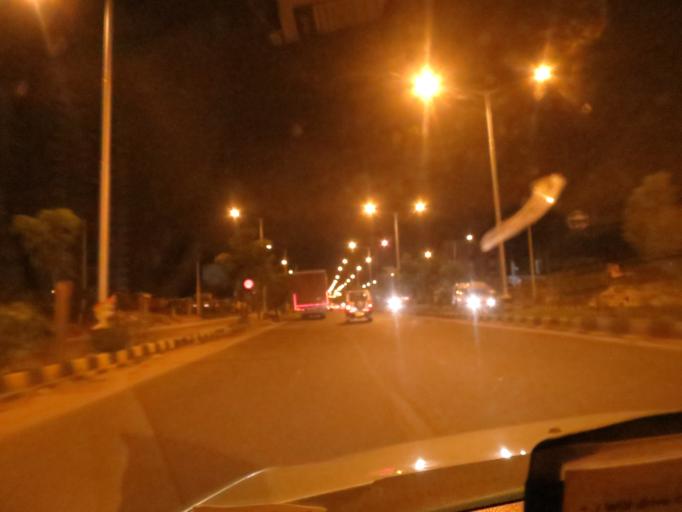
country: IN
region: Karnataka
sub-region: Bangalore Urban
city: Bangalore
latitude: 12.9933
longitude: 77.6858
